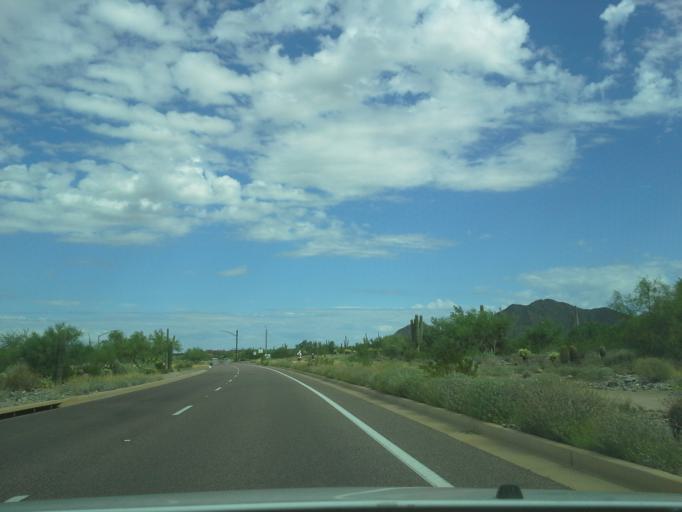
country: US
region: Arizona
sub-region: Maricopa County
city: Paradise Valley
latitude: 33.6460
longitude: -111.8615
